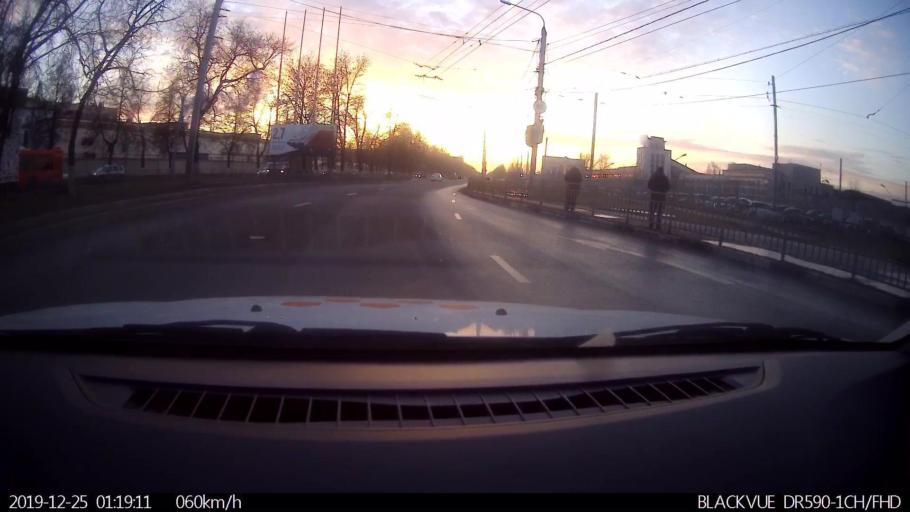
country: RU
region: Nizjnij Novgorod
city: Nizhniy Novgorod
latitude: 56.2572
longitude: 43.9020
